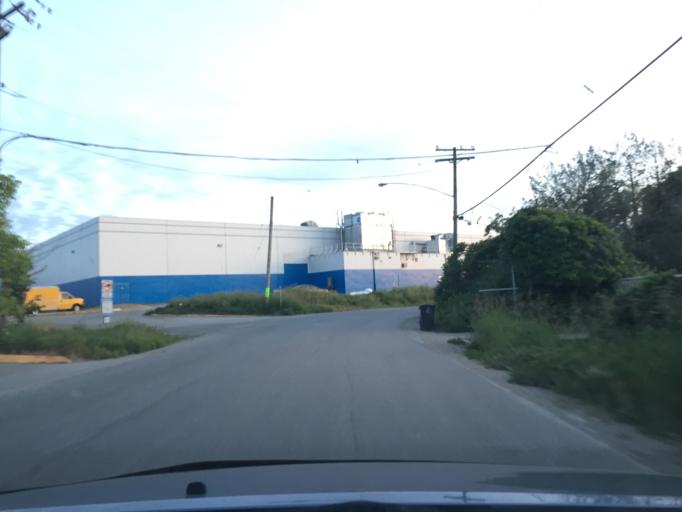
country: CA
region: British Columbia
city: Ladner
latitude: 49.1374
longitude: -123.0651
